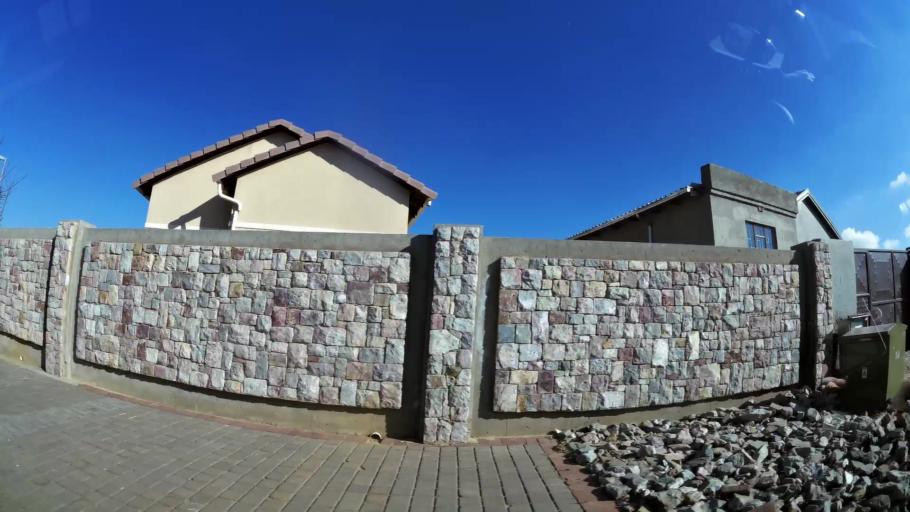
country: ZA
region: Gauteng
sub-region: City of Johannesburg Metropolitan Municipality
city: Roodepoort
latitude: -26.1582
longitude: 27.8359
